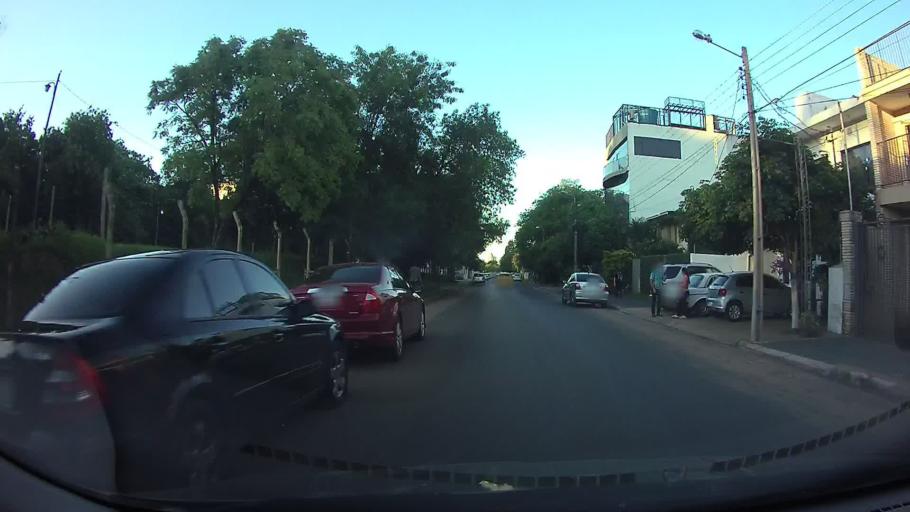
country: PY
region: Central
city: Fernando de la Mora
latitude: -25.3054
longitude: -57.5546
